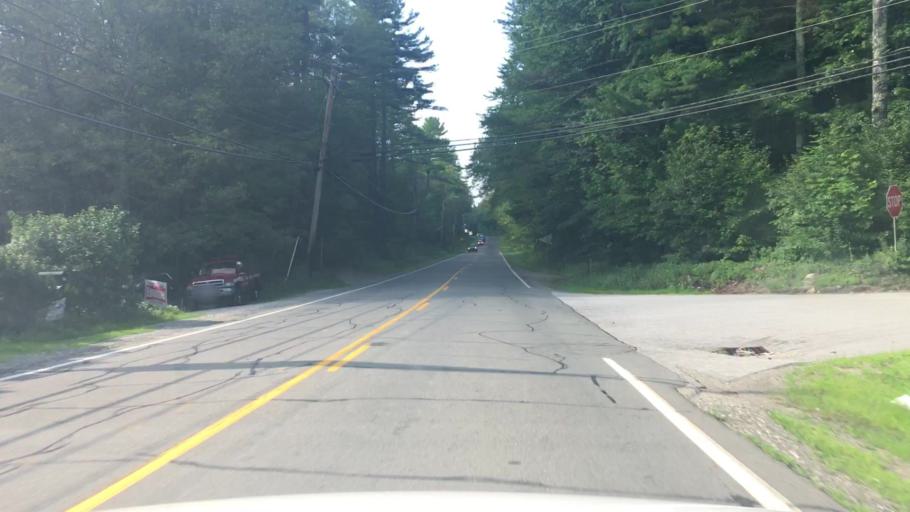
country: US
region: New Hampshire
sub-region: Rockingham County
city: Auburn
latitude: 42.9624
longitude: -71.3600
